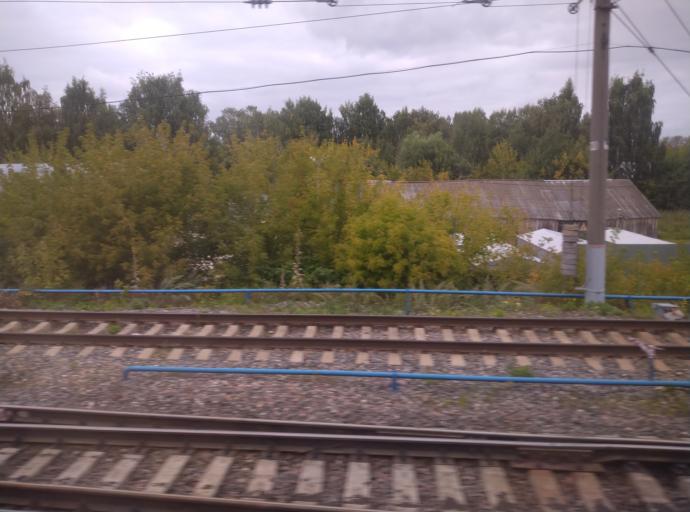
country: RU
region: Kostroma
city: Nerekhta
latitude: 57.4638
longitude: 40.5530
